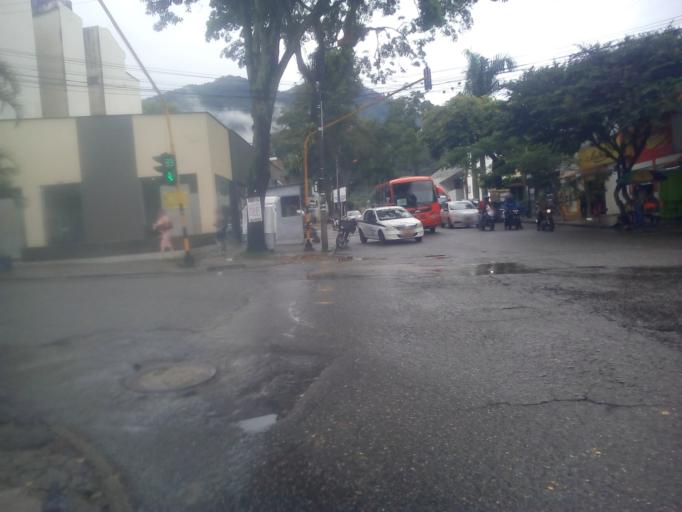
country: CO
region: Tolima
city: Ibague
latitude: 4.4474
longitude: -75.2410
